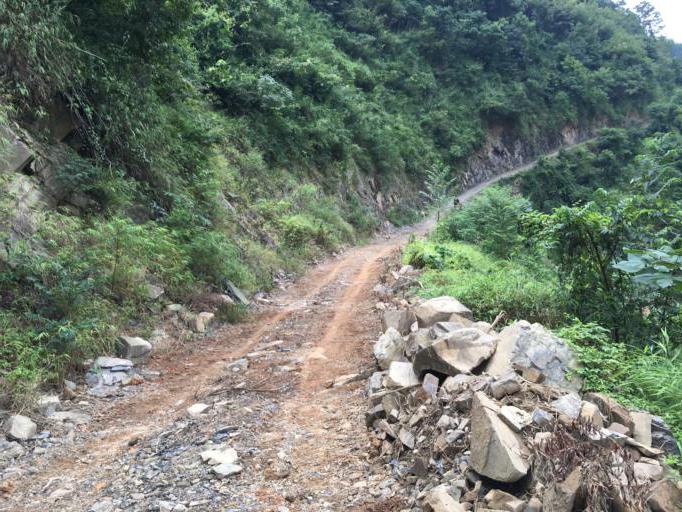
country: CN
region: Guangxi Zhuangzu Zizhiqu
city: Tongle
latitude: 25.3011
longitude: 106.1432
